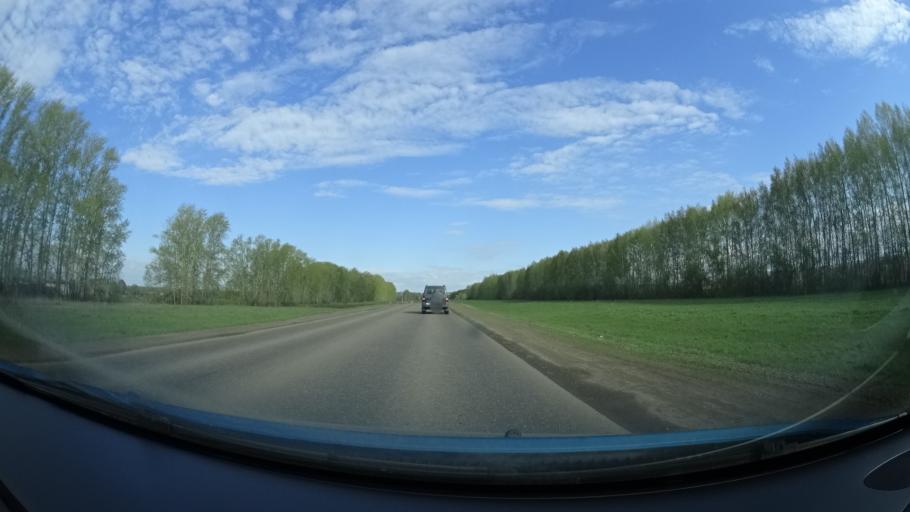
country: RU
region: Bashkortostan
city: Birsk
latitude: 55.2482
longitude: 55.7588
